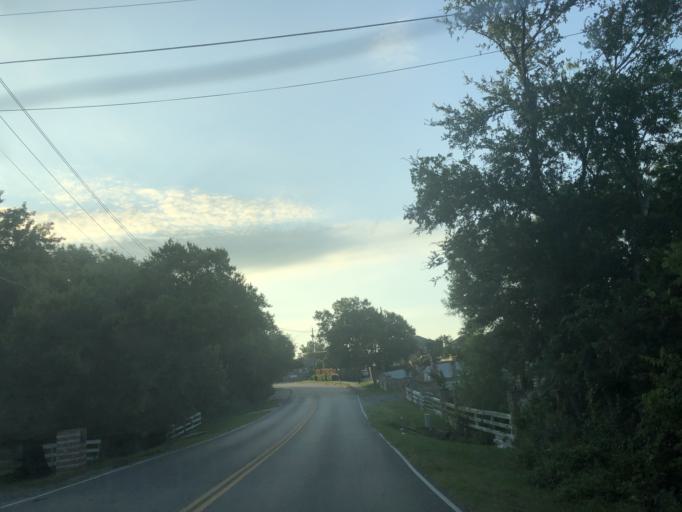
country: US
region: Texas
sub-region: Dallas County
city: Sunnyvale
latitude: 32.8367
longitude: -96.5681
